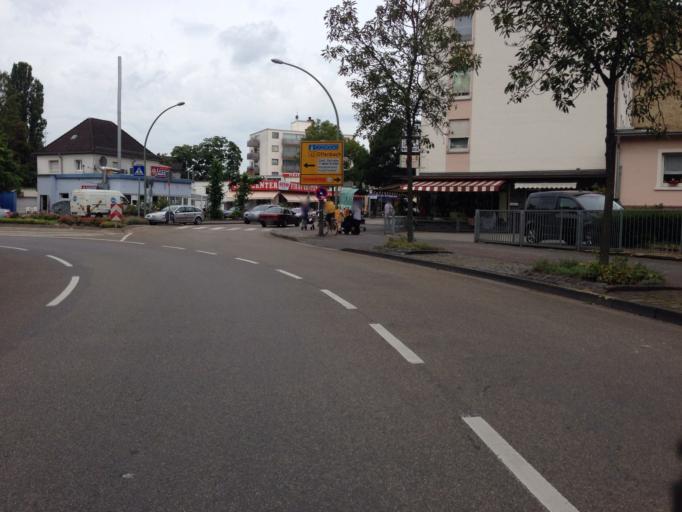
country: DE
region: Hesse
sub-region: Regierungsbezirk Darmstadt
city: Hanau am Main
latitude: 50.1268
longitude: 8.9284
